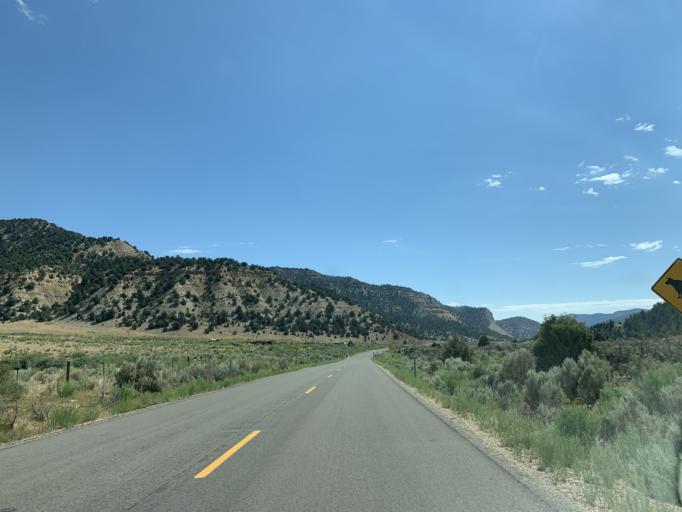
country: US
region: Utah
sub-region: Carbon County
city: East Carbon City
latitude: 39.7744
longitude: -110.5122
